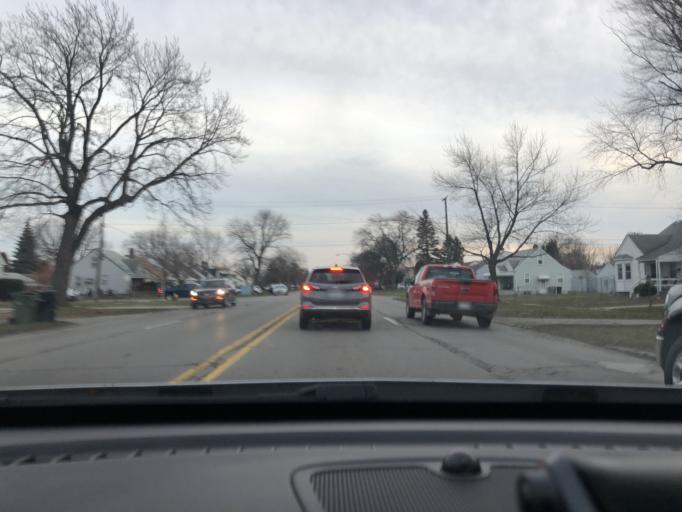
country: US
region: Michigan
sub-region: Wayne County
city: Allen Park
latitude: 42.2595
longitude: -83.2314
